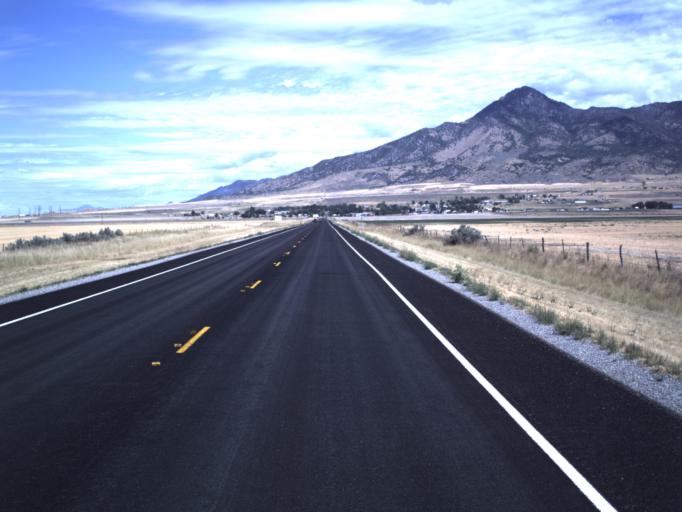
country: US
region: Utah
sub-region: Box Elder County
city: Garland
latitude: 41.8502
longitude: -112.1464
